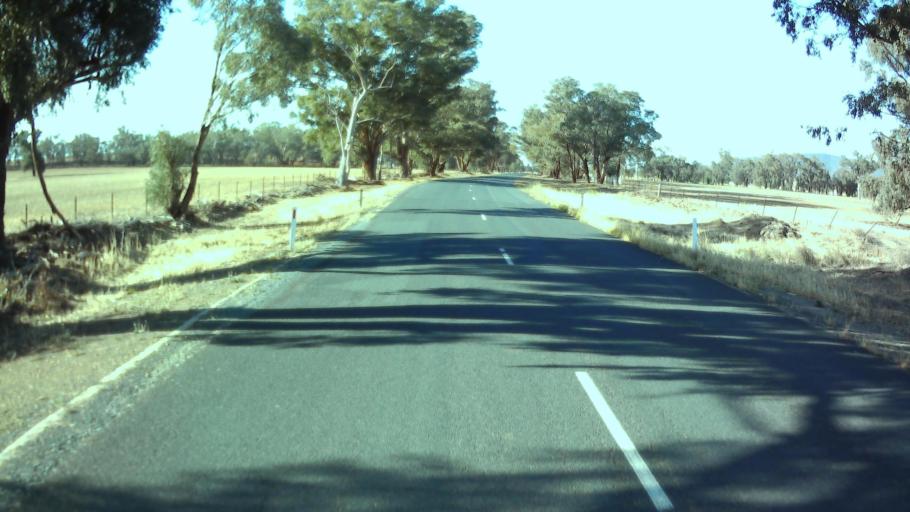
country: AU
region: New South Wales
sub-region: Weddin
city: Grenfell
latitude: -33.9381
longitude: 148.1373
